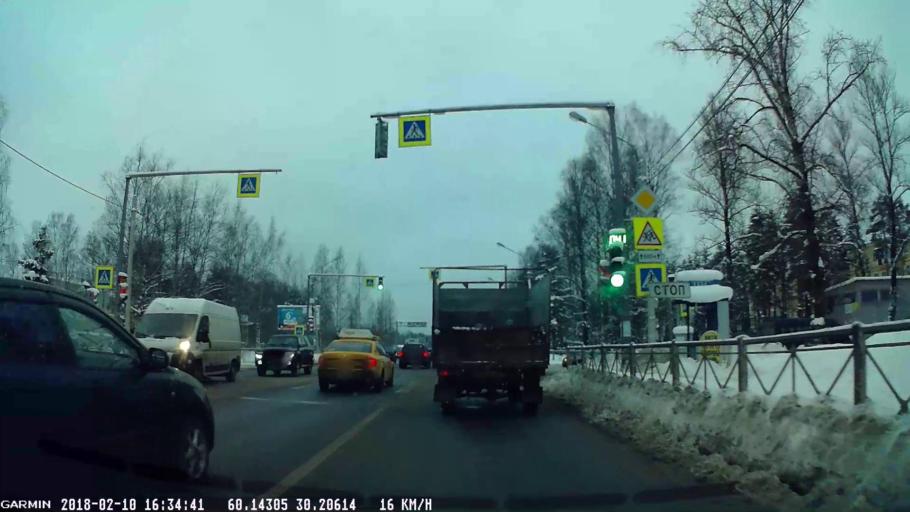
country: RU
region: Leningrad
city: Sertolovo
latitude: 60.1435
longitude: 30.2056
